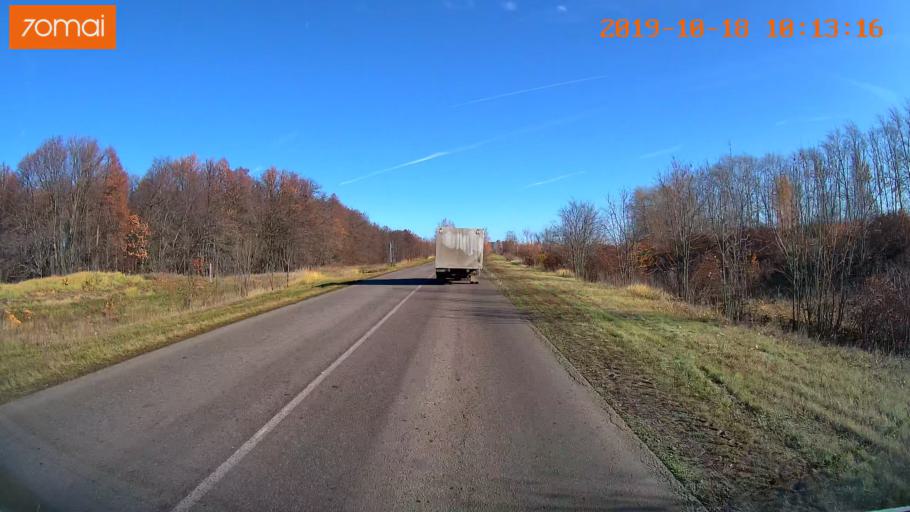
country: RU
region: Tula
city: Kurkino
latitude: 53.4006
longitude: 38.5190
